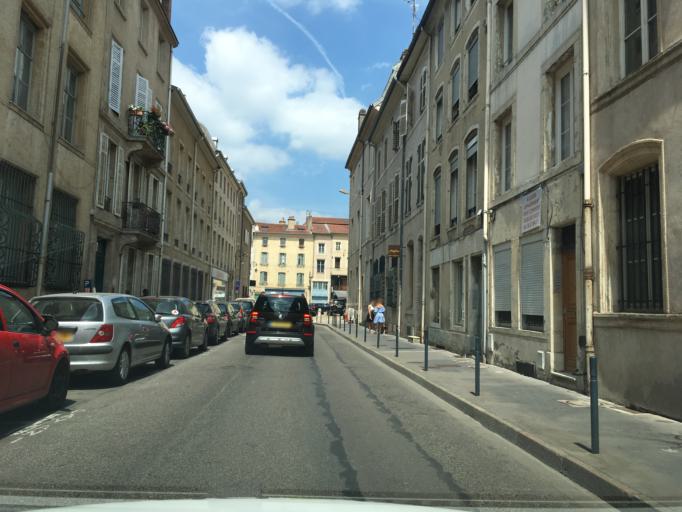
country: FR
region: Lorraine
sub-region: Departement de Meurthe-et-Moselle
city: Nancy
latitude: 48.6909
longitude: 6.1855
